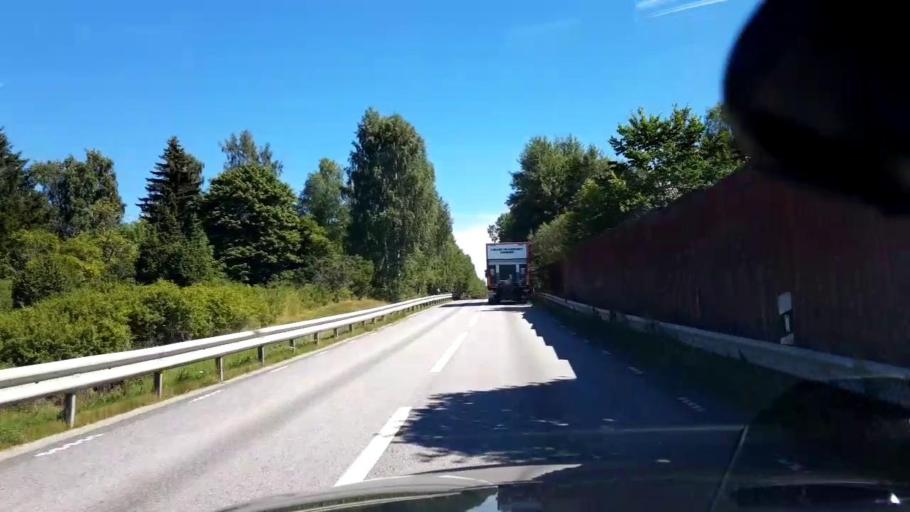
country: SE
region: Stockholm
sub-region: Sigtuna Kommun
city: Sigtuna
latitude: 59.6505
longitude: 17.6481
